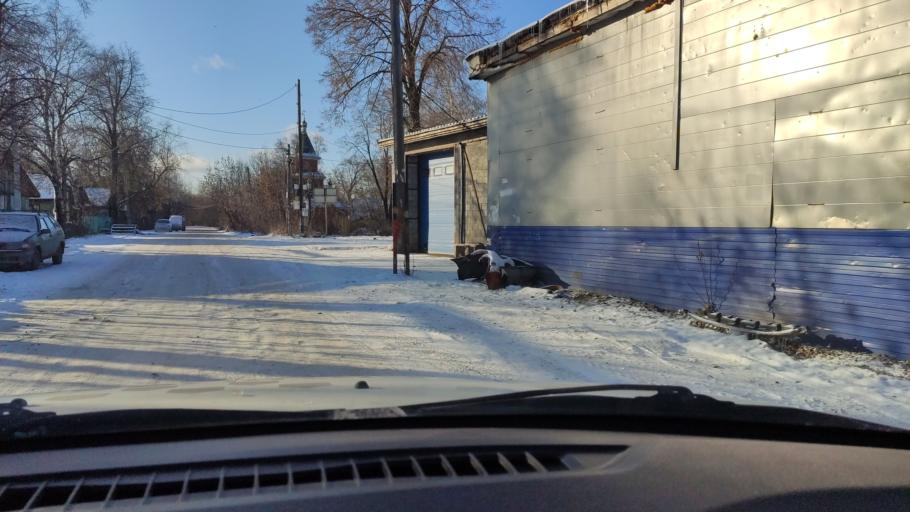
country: RU
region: Perm
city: Kondratovo
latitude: 58.0068
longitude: 56.1268
